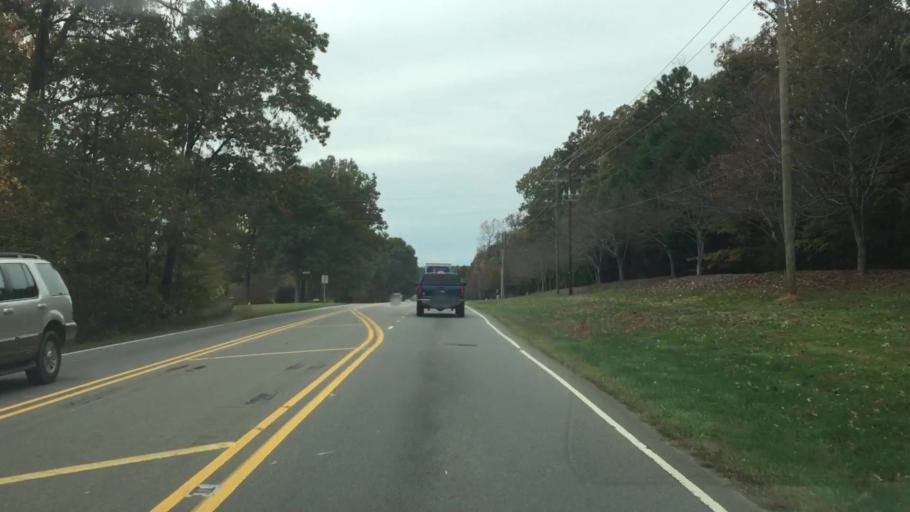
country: US
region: North Carolina
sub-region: Iredell County
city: Mooresville
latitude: 35.6043
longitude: -80.7779
